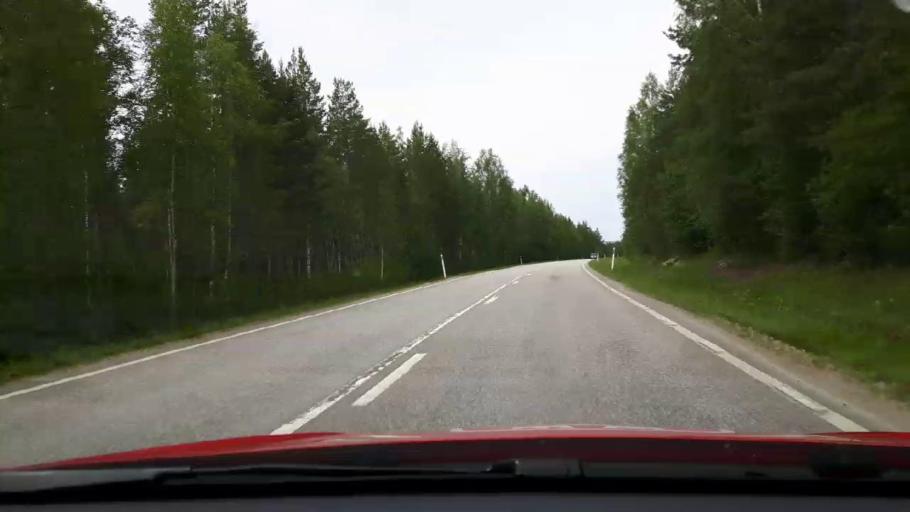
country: SE
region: Jaemtland
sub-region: Harjedalens Kommun
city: Sveg
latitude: 62.1028
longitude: 14.2080
